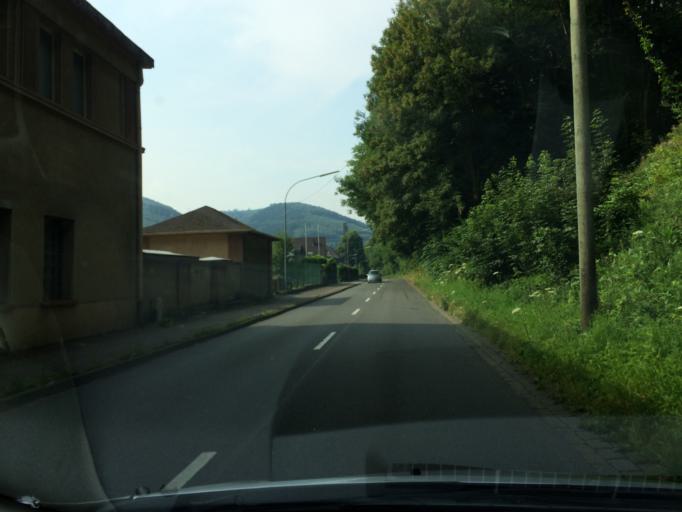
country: DE
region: North Rhine-Westphalia
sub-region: Regierungsbezirk Arnsberg
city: Nachrodt-Wiblingwerde
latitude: 51.3546
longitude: 7.6019
